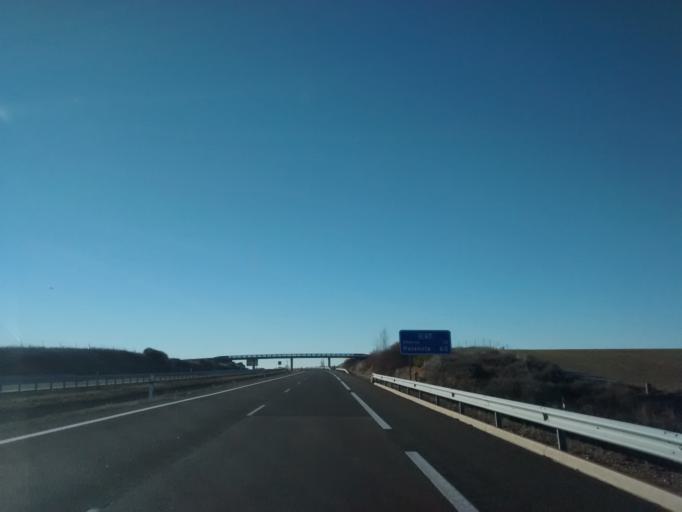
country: ES
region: Castille and Leon
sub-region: Provincia de Palencia
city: Santa Cruz de Boedo
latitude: 42.5326
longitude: -4.3822
